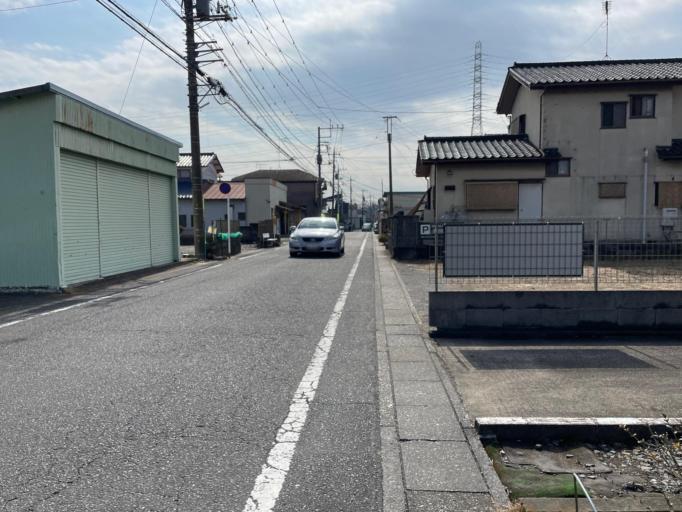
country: JP
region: Saitama
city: Yoshikawa
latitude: 35.8624
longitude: 139.8408
